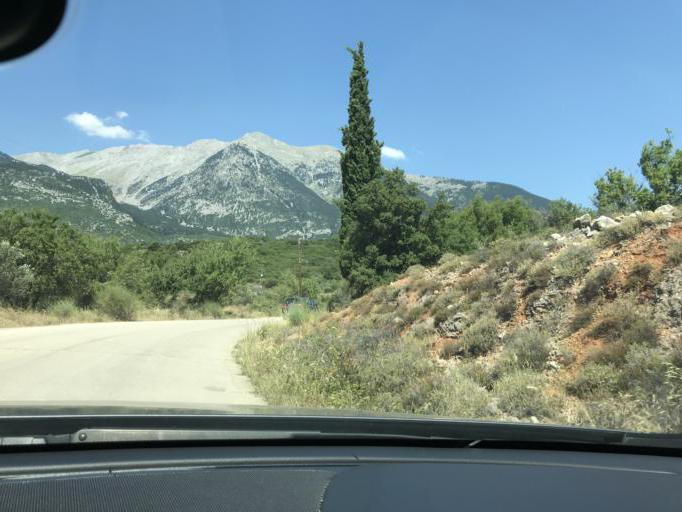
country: GR
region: Central Greece
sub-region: Nomos Voiotias
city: Distomo
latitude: 38.5107
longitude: 22.7233
